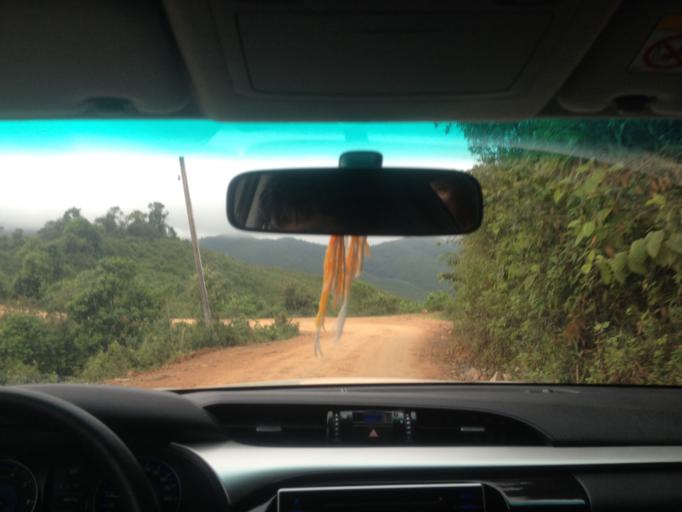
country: TH
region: Nan
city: Chaloem Phra Kiat
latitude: 19.9942
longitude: 101.1349
